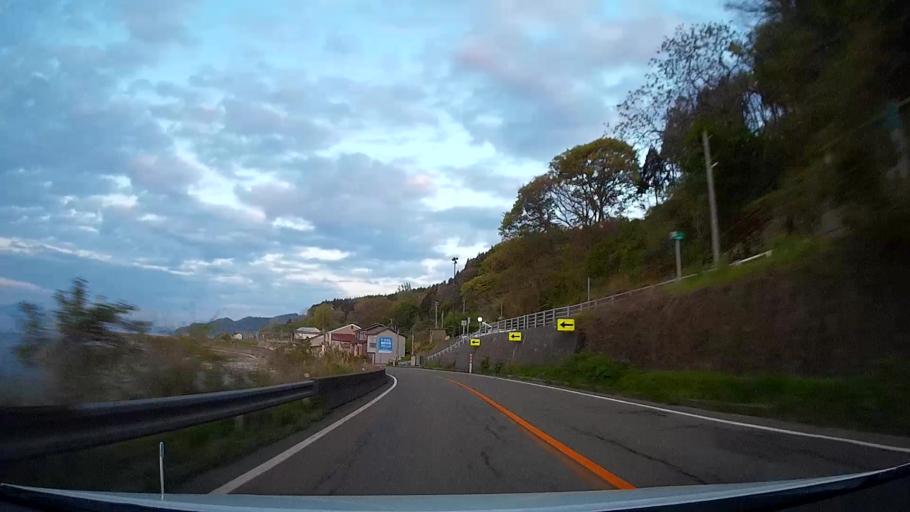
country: JP
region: Niigata
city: Joetsu
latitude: 37.1637
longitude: 138.1326
